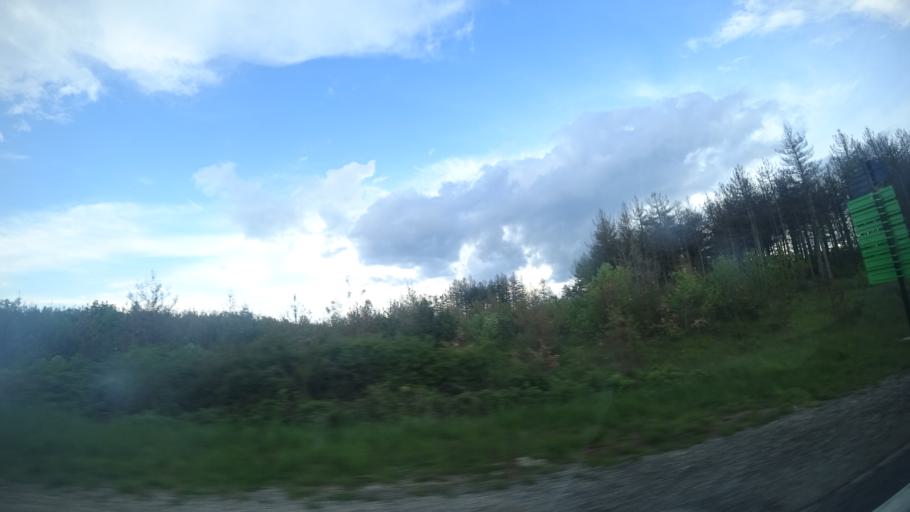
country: FR
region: Midi-Pyrenees
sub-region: Departement de l'Aveyron
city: Millau
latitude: 44.1991
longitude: 3.0176
